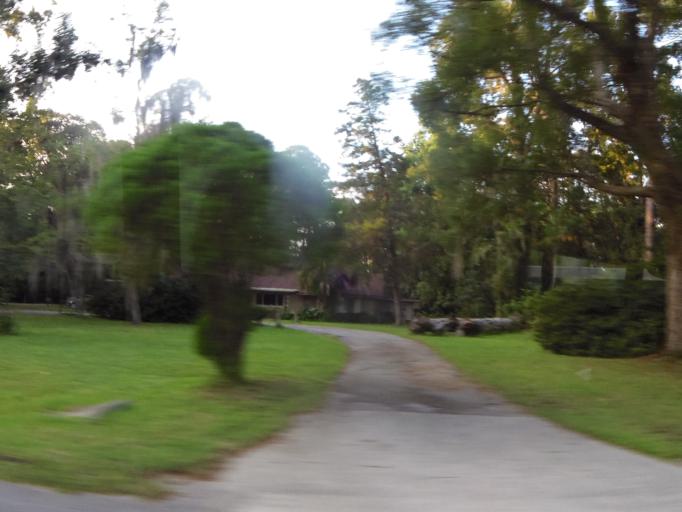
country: US
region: Florida
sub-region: Saint Johns County
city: Fruit Cove
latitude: 30.1796
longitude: -81.6327
